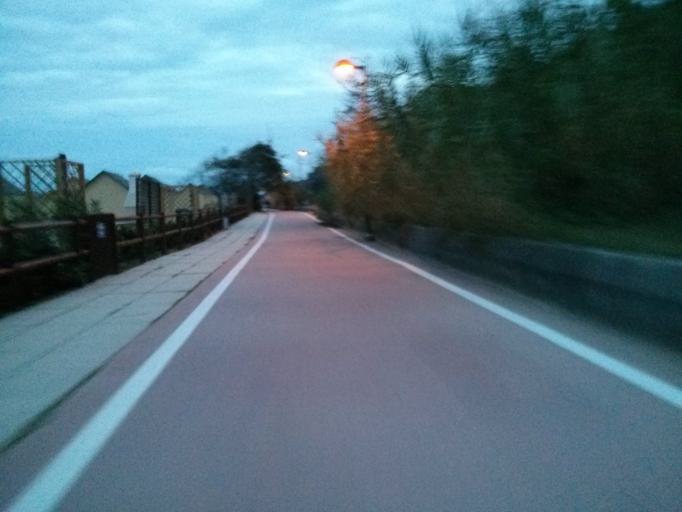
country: IT
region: The Marches
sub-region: Provincia di Pesaro e Urbino
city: Fenile
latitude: 43.8883
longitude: 12.9525
